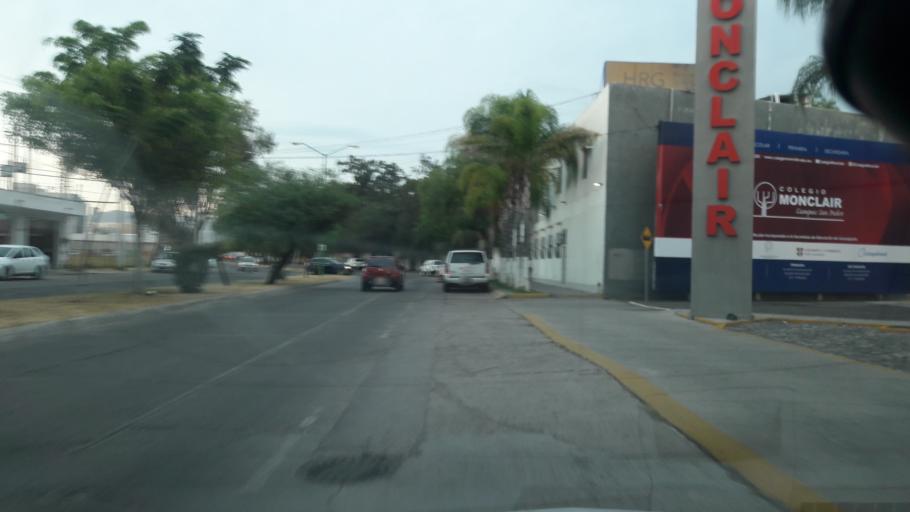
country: MX
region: Guanajuato
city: Leon
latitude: 21.1052
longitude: -101.6444
